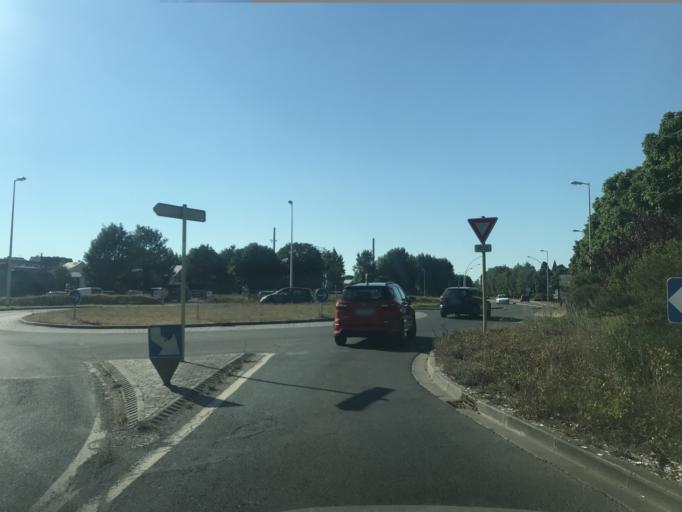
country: FR
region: Lower Normandy
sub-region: Departement du Calvados
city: Trouville-sur-Mer
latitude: 49.3564
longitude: 0.0861
